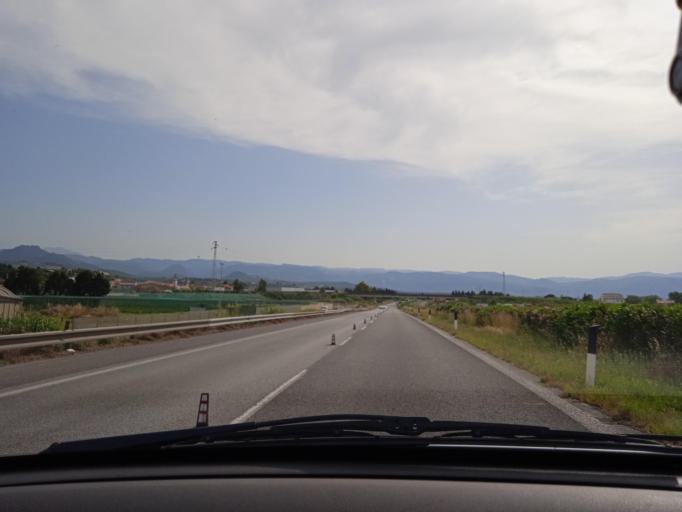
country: IT
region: Sicily
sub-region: Messina
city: Terme
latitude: 38.1475
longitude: 15.1711
